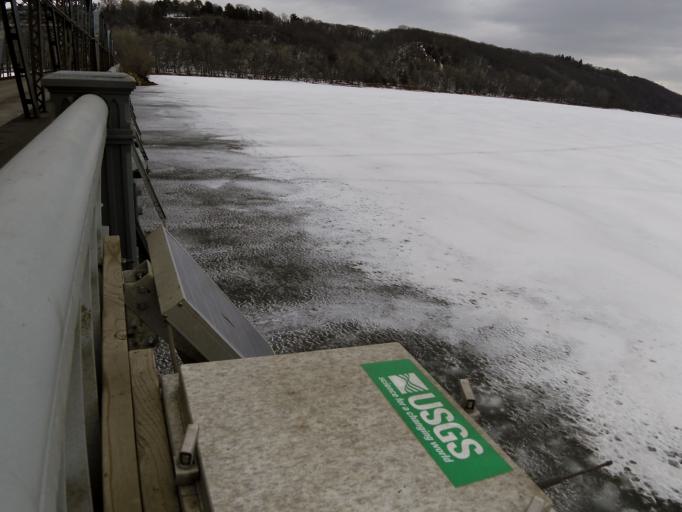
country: US
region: Minnesota
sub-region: Washington County
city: Stillwater
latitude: 45.0567
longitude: -92.8023
